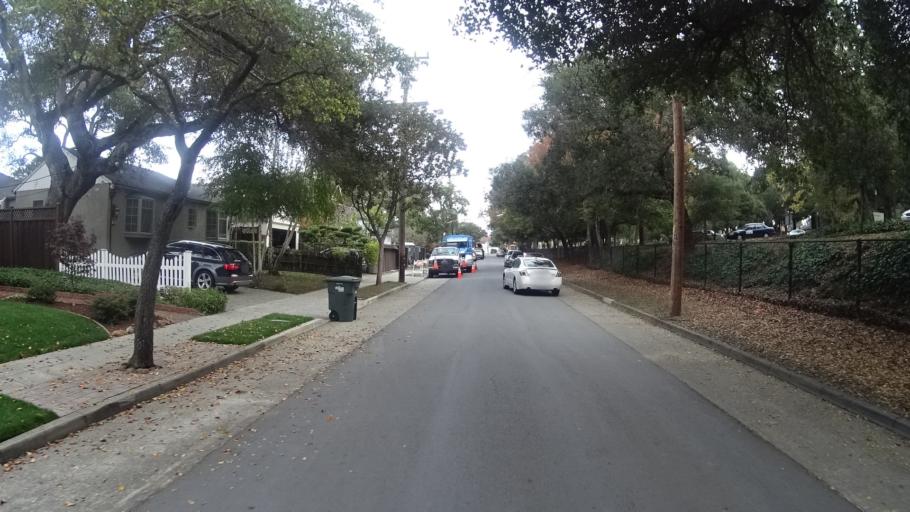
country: US
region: California
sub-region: San Mateo County
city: Hillsborough
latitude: 37.5848
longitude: -122.3818
